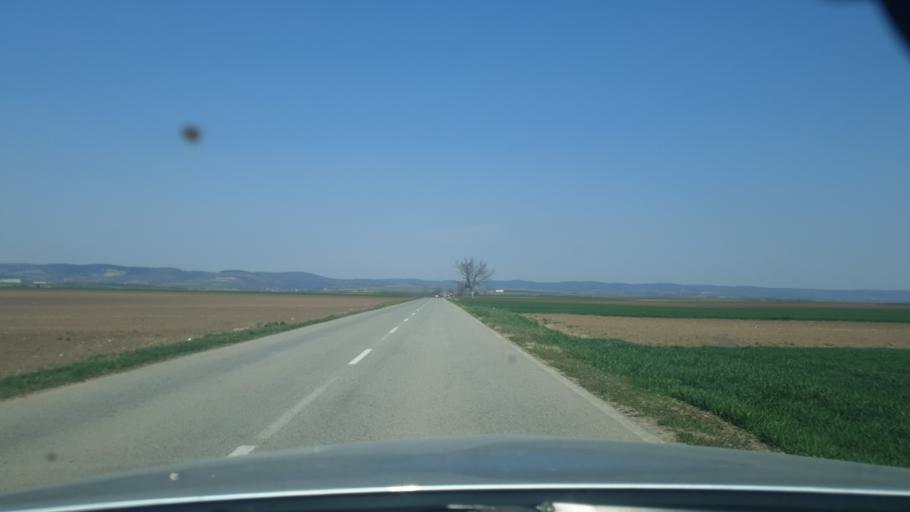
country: RS
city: Vrdnik
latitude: 45.0558
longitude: 19.7663
